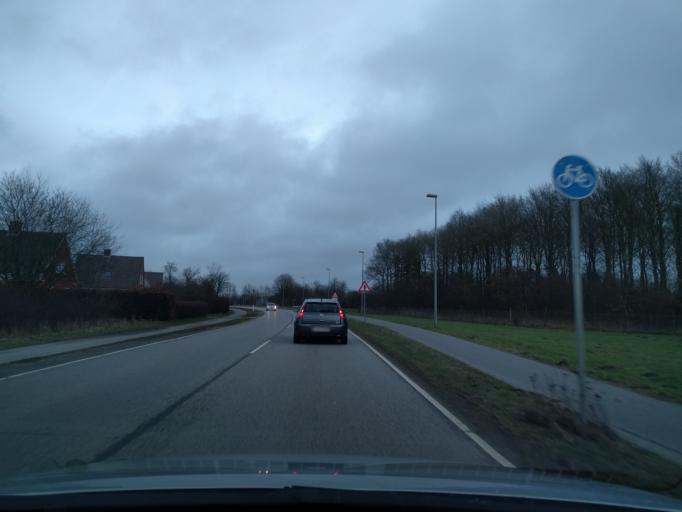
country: DK
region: South Denmark
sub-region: Haderslev Kommune
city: Vojens
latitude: 55.2420
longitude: 9.2598
